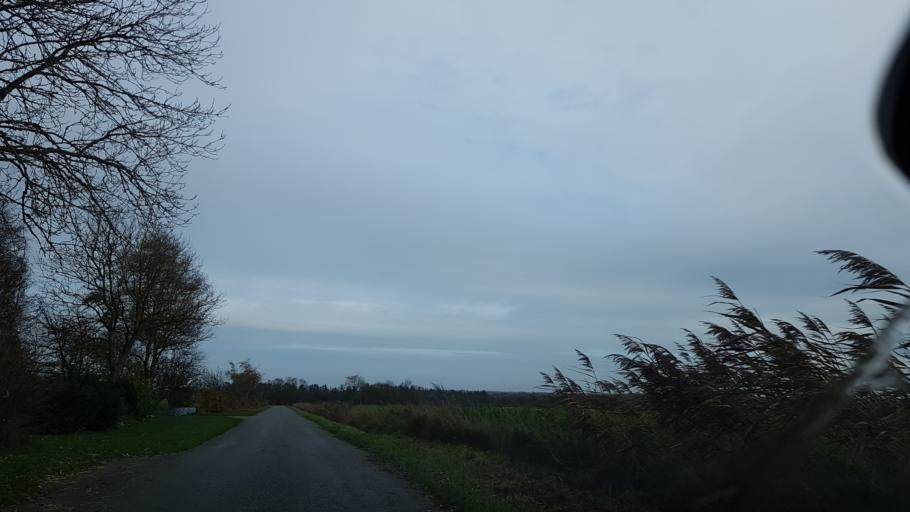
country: DK
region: South Denmark
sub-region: Tonder Kommune
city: Sherrebek
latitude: 55.2240
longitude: 8.8738
